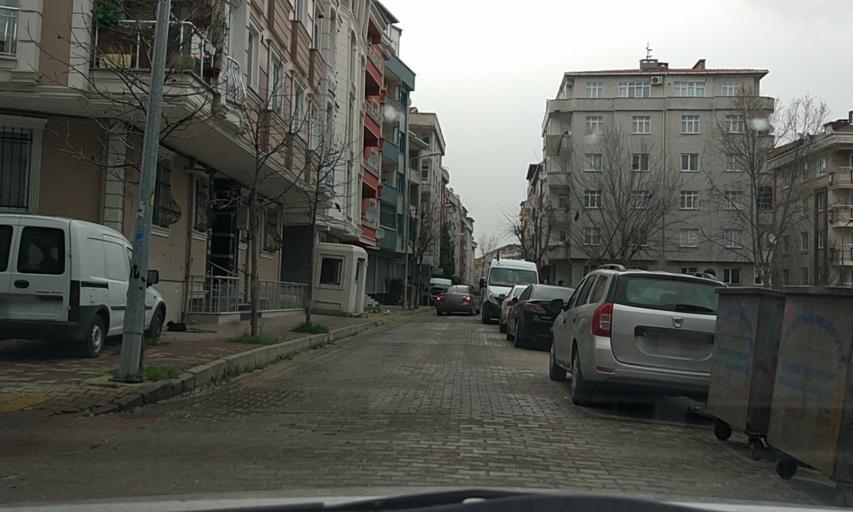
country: TR
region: Istanbul
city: Bagcilar
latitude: 41.0195
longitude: 28.8321
